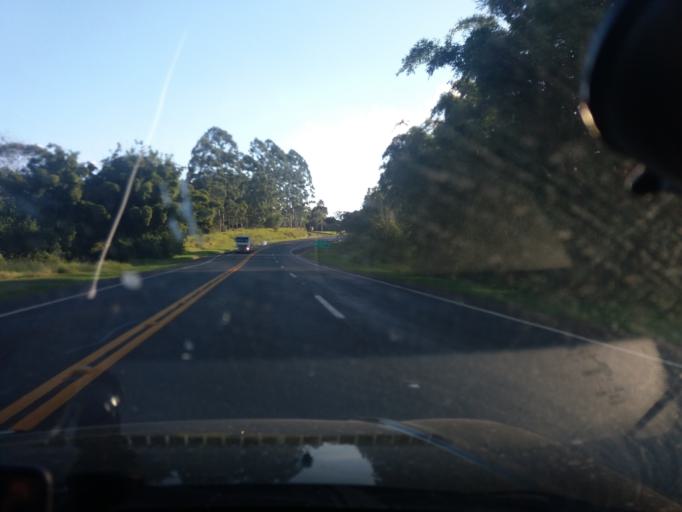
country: BR
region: Sao Paulo
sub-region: Buri
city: Buri
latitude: -23.9286
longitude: -48.6650
